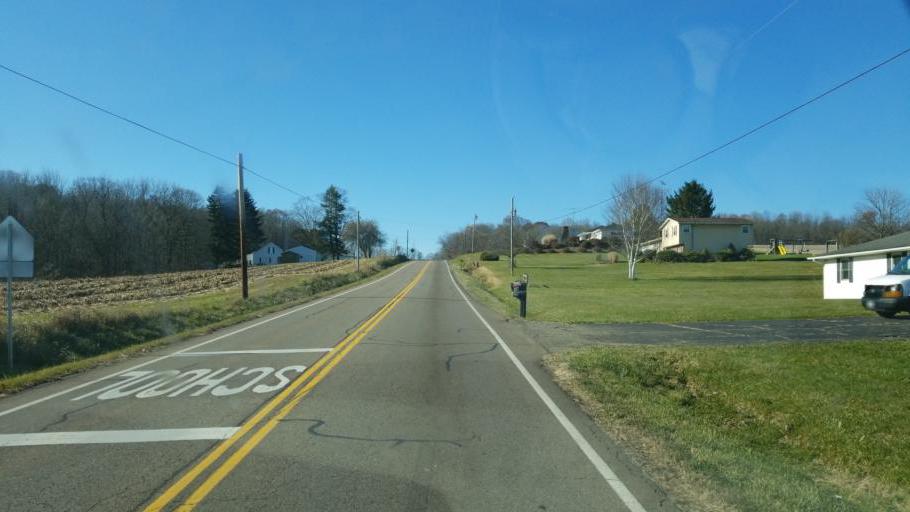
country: US
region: Ohio
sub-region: Knox County
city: Gambier
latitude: 40.4086
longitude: -82.3333
